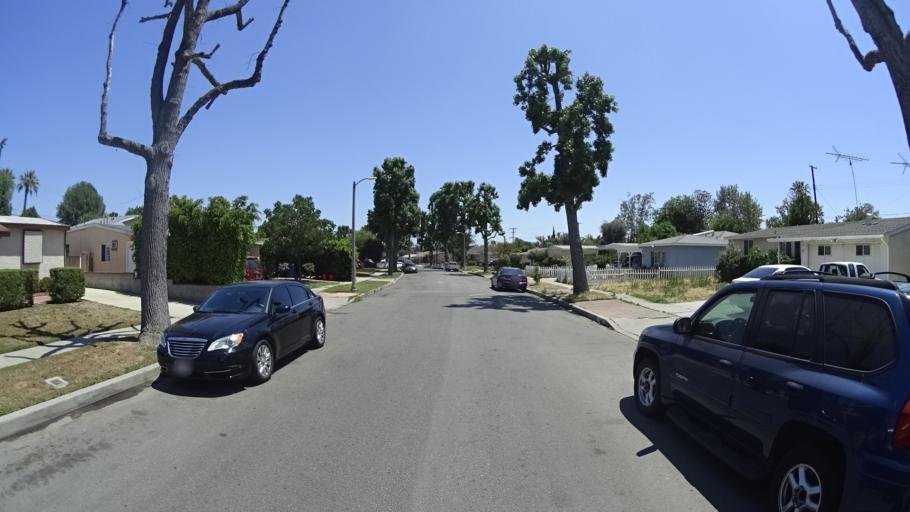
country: US
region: California
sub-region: Los Angeles County
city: Van Nuys
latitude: 34.2140
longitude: -118.4364
